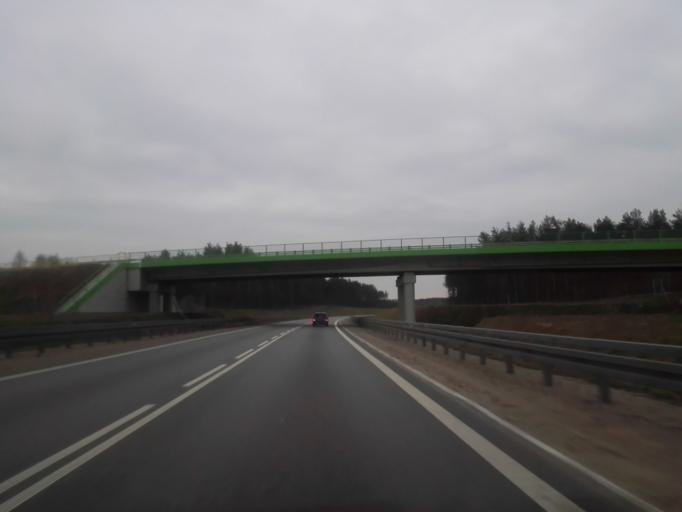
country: PL
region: Podlasie
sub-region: Powiat kolnenski
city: Stawiski
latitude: 53.3639
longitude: 22.1580
